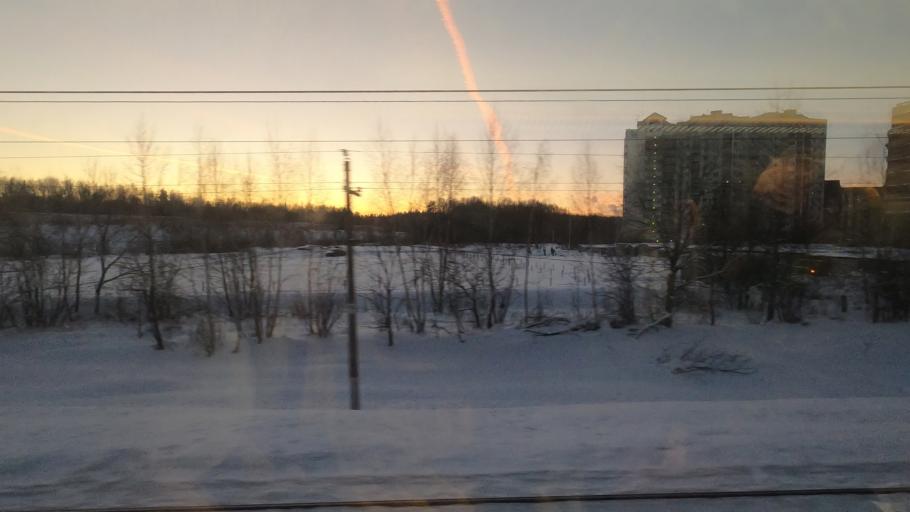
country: RU
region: Moskovskaya
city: Lobnya
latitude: 56.0000
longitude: 37.4912
